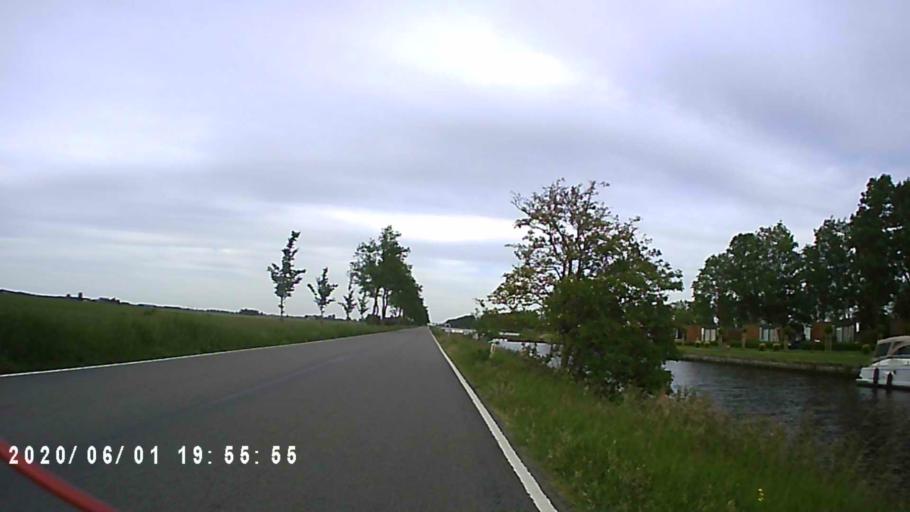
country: NL
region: Friesland
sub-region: Gemeente Achtkarspelen
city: Surhuizum
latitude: 53.2392
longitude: 6.2208
